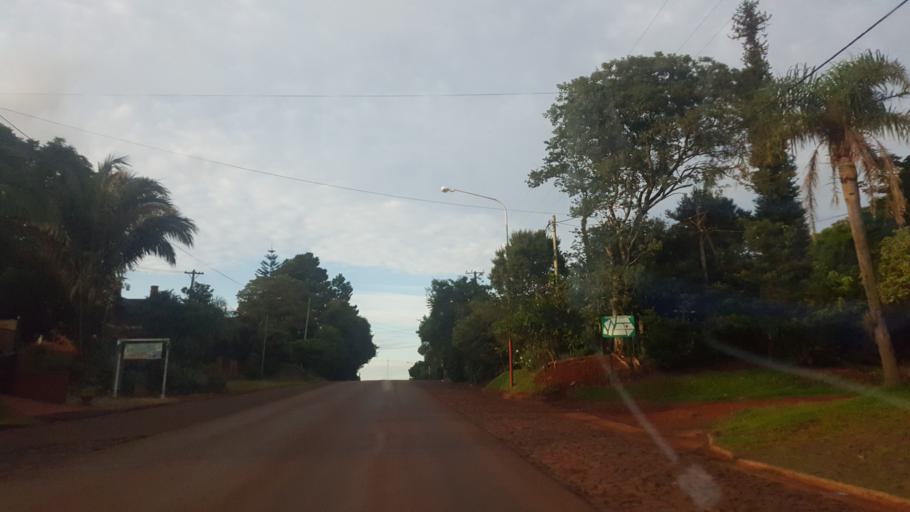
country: AR
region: Misiones
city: Dos de Mayo
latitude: -27.0160
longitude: -54.6851
